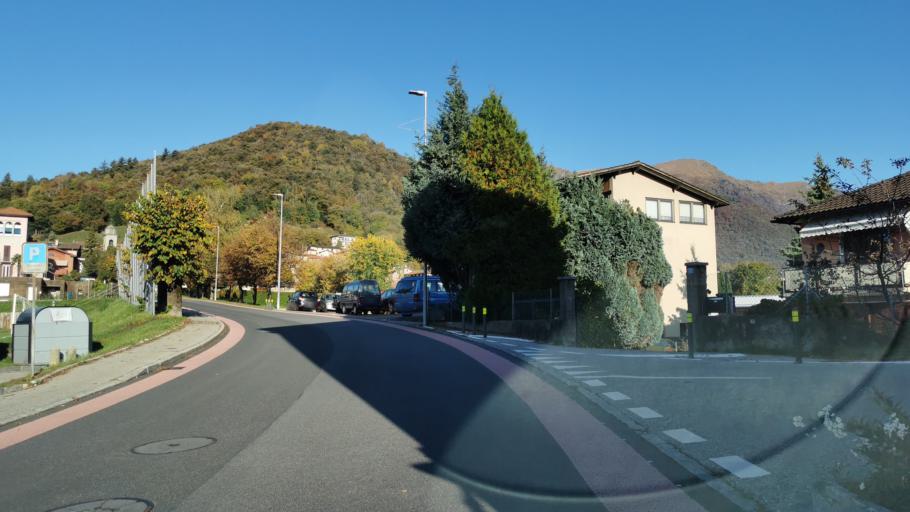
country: CH
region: Ticino
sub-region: Lugano District
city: Pura
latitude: 46.0089
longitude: 8.8591
